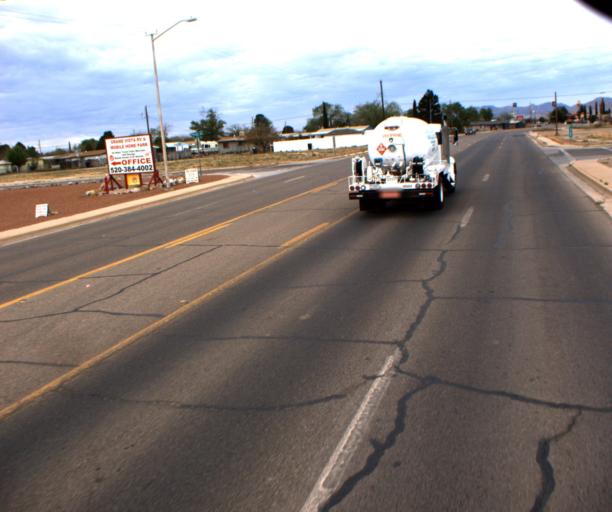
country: US
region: Arizona
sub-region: Cochise County
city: Willcox
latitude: 32.2641
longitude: -109.8334
